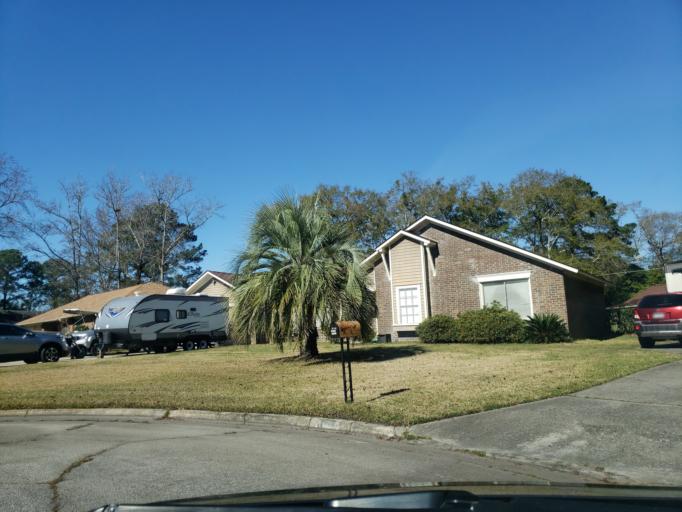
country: US
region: Georgia
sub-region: Chatham County
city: Montgomery
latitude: 31.9983
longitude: -81.1416
